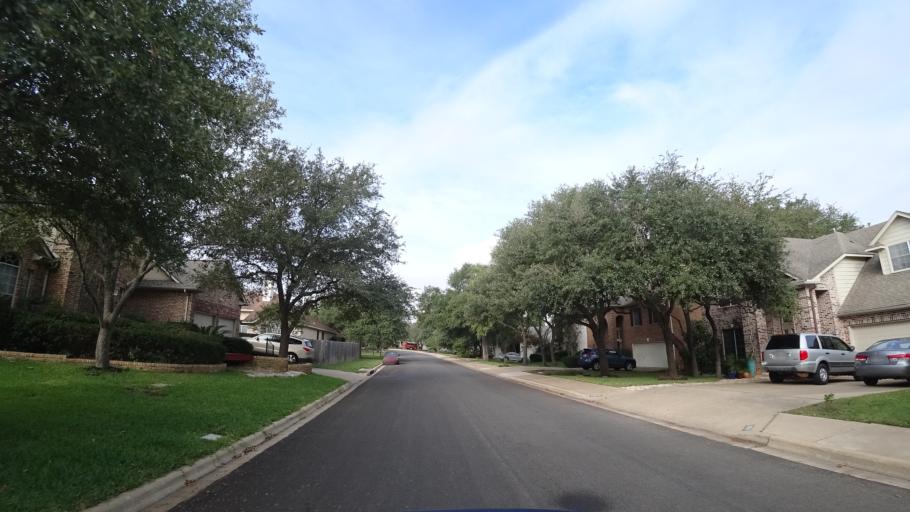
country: US
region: Texas
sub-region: Travis County
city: Shady Hollow
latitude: 30.1891
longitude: -97.8819
